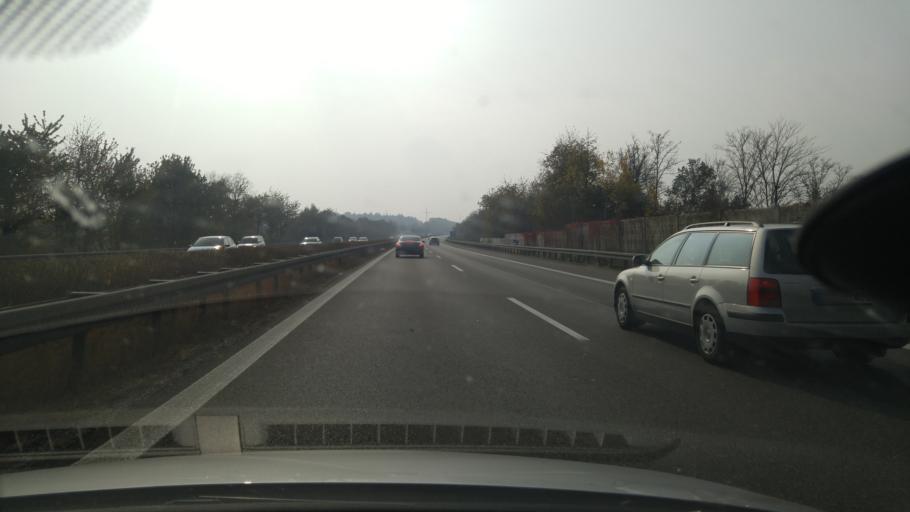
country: DE
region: Baden-Wuerttemberg
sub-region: Regierungsbezirk Stuttgart
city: Motzingen
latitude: 48.4614
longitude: 8.7808
